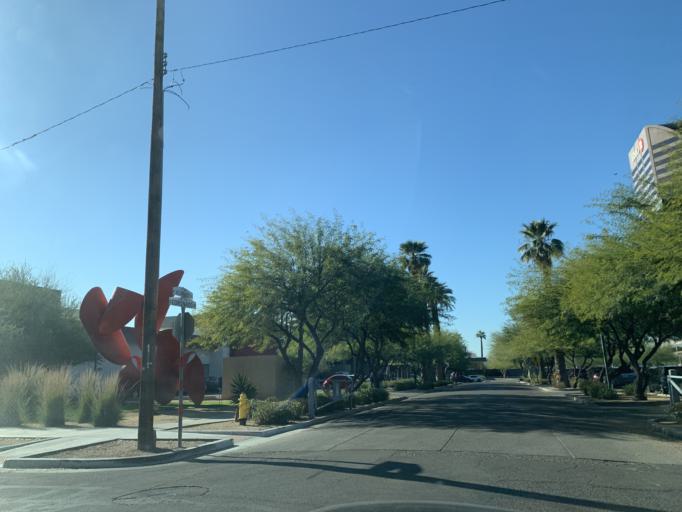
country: US
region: Arizona
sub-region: Maricopa County
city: Phoenix
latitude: 33.4676
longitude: -112.0715
